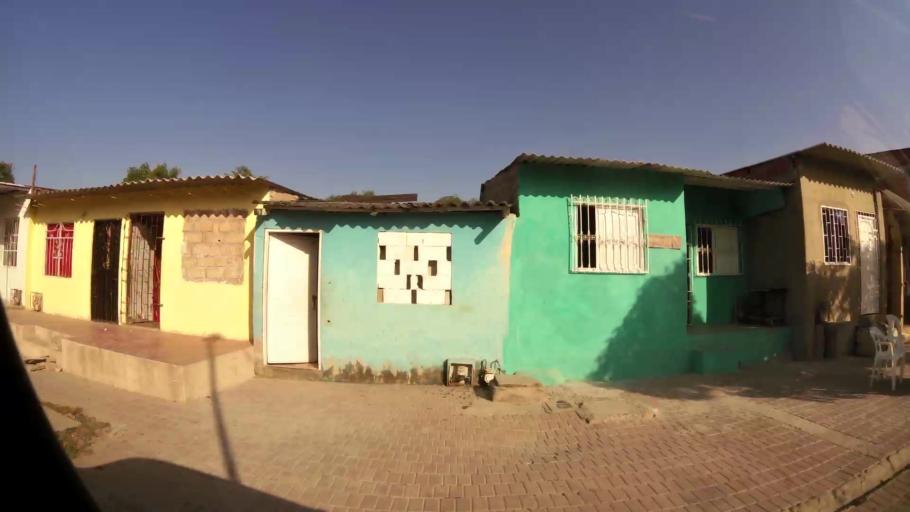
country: CO
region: Bolivar
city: Cartagena
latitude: 10.4136
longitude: -75.4958
